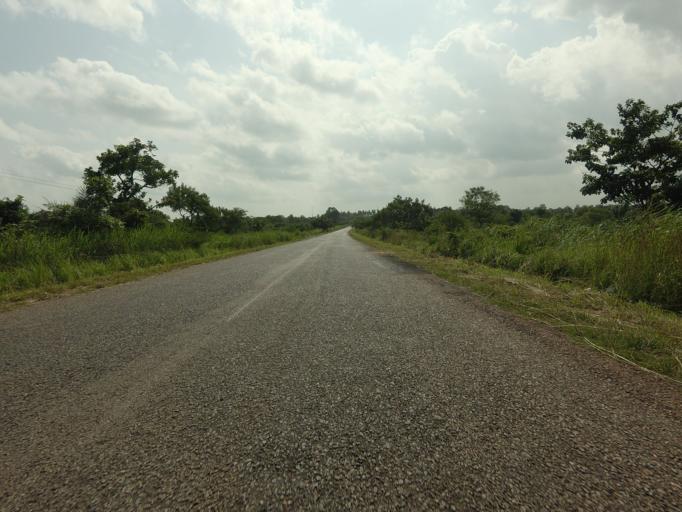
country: GH
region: Volta
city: Ho
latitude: 6.4102
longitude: 0.7637
